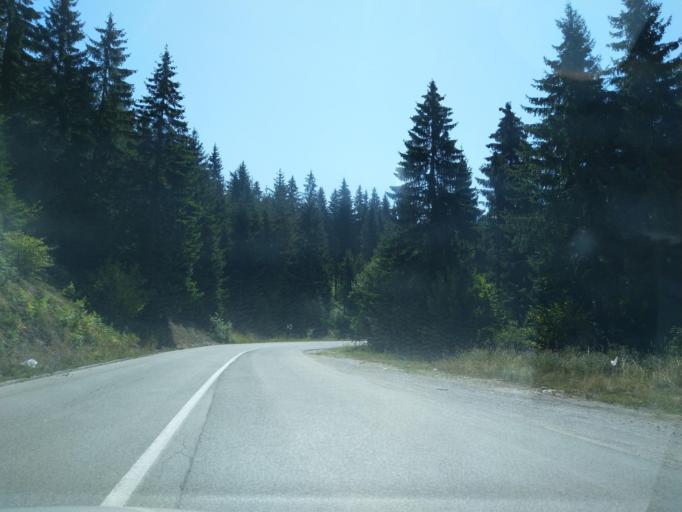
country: RS
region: Central Serbia
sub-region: Zlatiborski Okrug
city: Nova Varos
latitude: 43.3540
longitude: 19.8557
